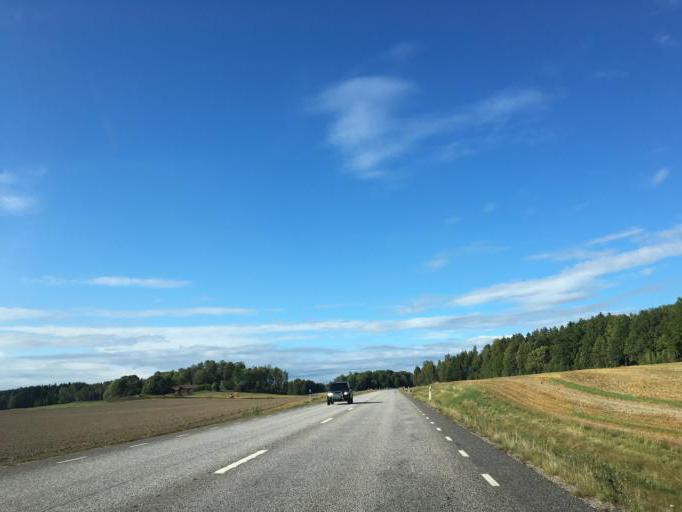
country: SE
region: Soedermanland
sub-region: Nykopings Kommun
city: Nykoping
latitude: 58.7985
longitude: 16.9513
